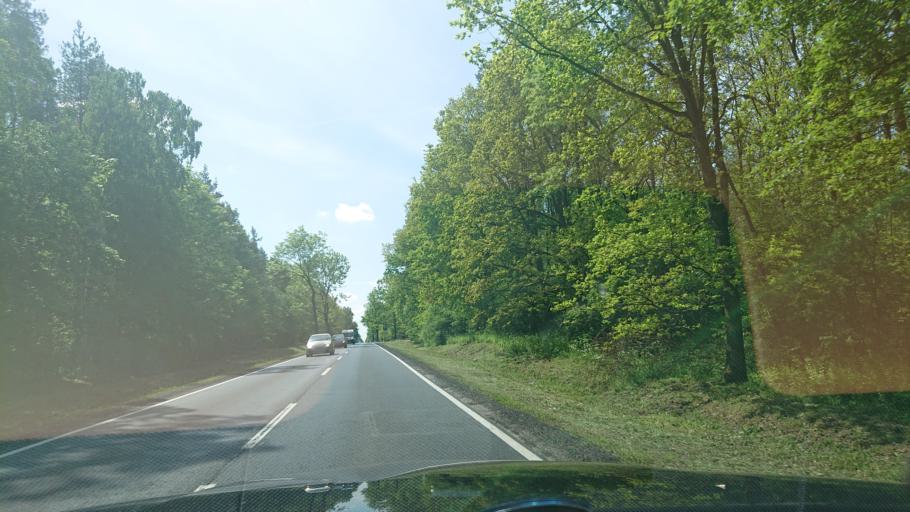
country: PL
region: Greater Poland Voivodeship
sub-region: Powiat gnieznienski
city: Gniezno
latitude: 52.4911
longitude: 17.5939
